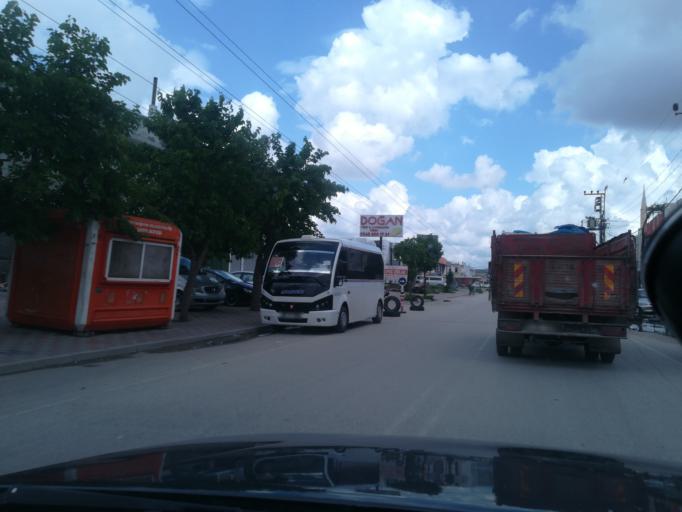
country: TR
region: Adana
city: Yuregir
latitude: 36.9769
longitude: 35.3856
